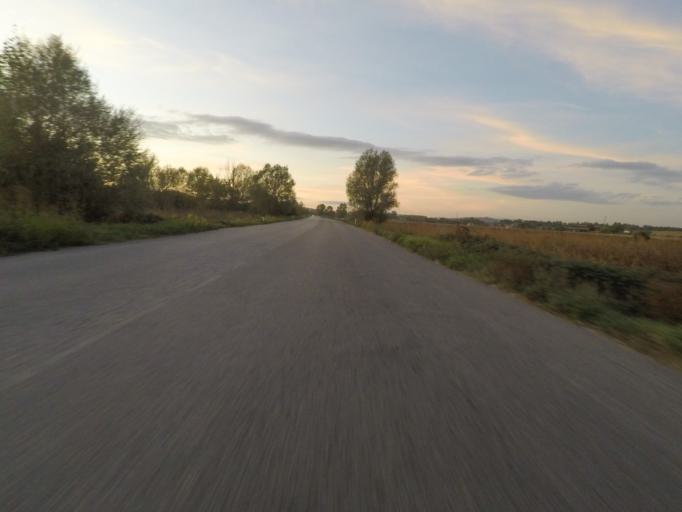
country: IT
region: Tuscany
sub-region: Provincia di Siena
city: Sinalunga
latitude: 43.2150
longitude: 11.7615
